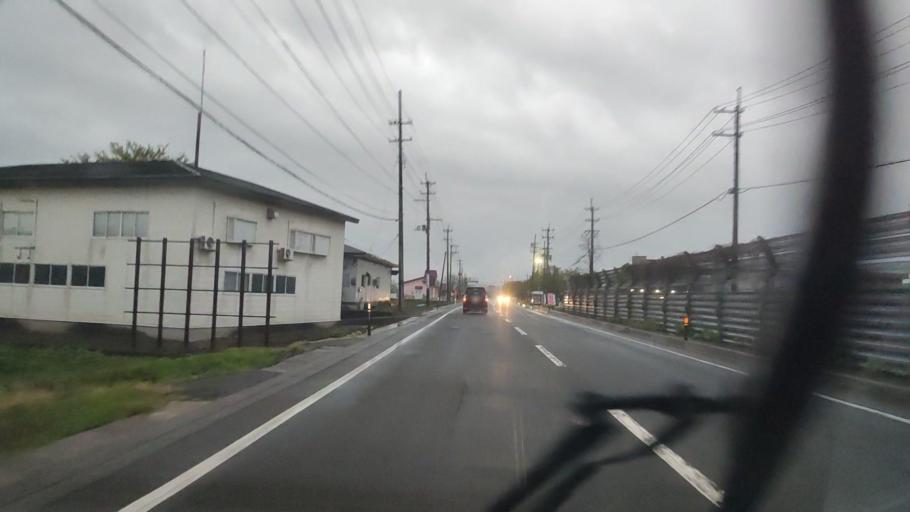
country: JP
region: Akita
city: Omagari
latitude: 39.5247
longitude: 140.3774
